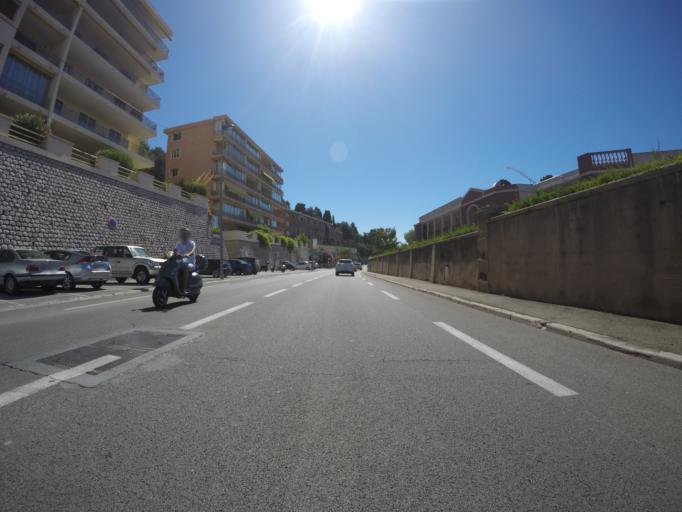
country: FR
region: Provence-Alpes-Cote d'Azur
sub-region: Departement des Alpes-Maritimes
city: Beaulieu-sur-Mer
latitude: 43.7034
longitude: 7.3234
